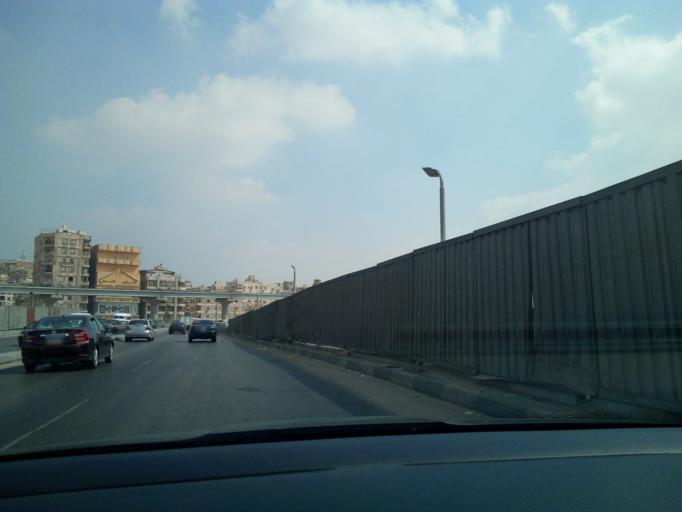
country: EG
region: Muhafazat al Qalyubiyah
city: Al Khankah
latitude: 30.1409
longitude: 31.4008
